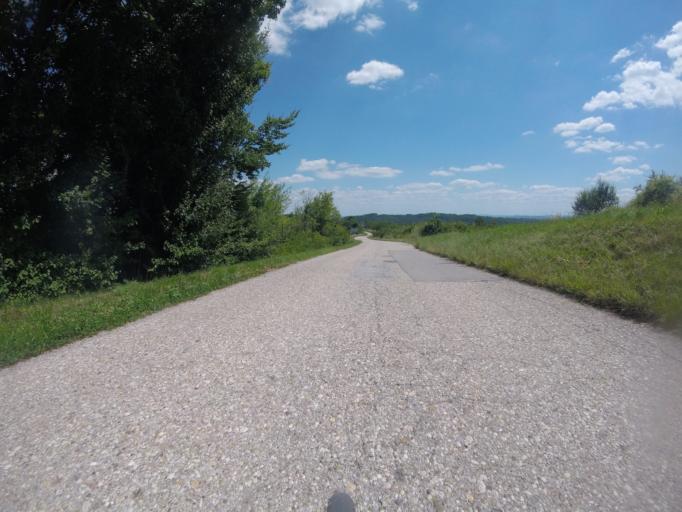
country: HR
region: Karlovacka
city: Ozalj
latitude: 45.6757
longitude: 15.4575
